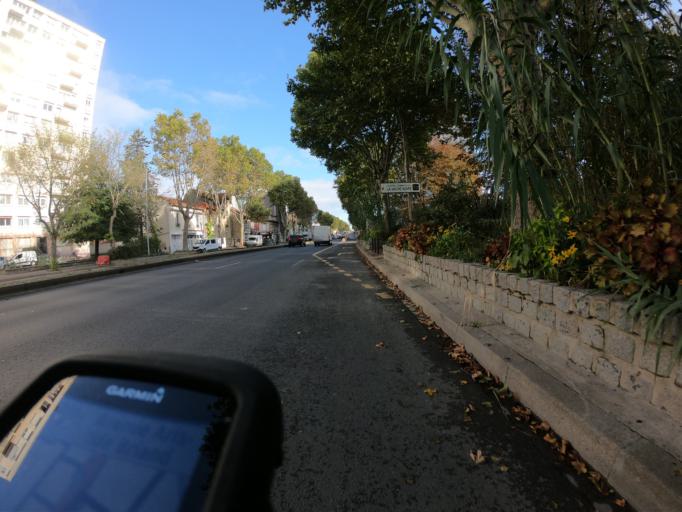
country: FR
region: Ile-de-France
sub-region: Departement des Hauts-de-Seine
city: Bourg-la-Reine
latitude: 48.7882
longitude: 2.3190
